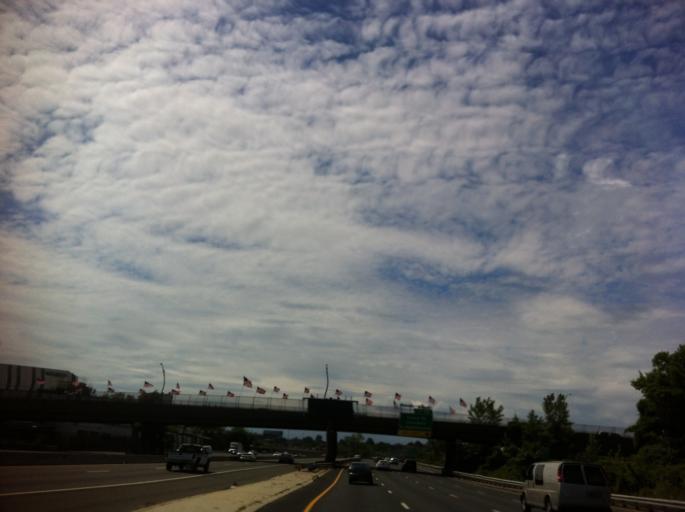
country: US
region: New Jersey
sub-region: Bergen County
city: Bogota
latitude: 40.8672
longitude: -74.0364
